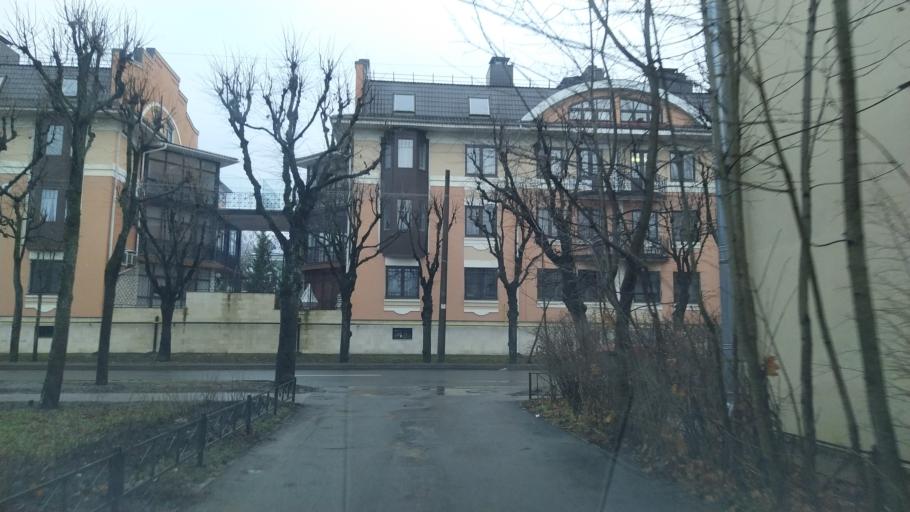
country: RU
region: St.-Petersburg
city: Pushkin
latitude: 59.7203
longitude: 30.4164
